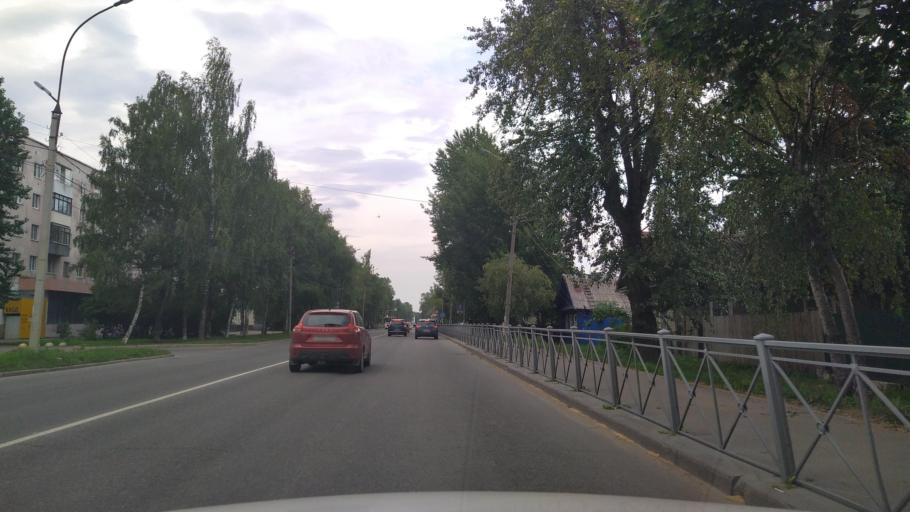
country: RU
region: Novgorod
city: Velikiy Novgorod
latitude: 58.5173
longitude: 31.2480
